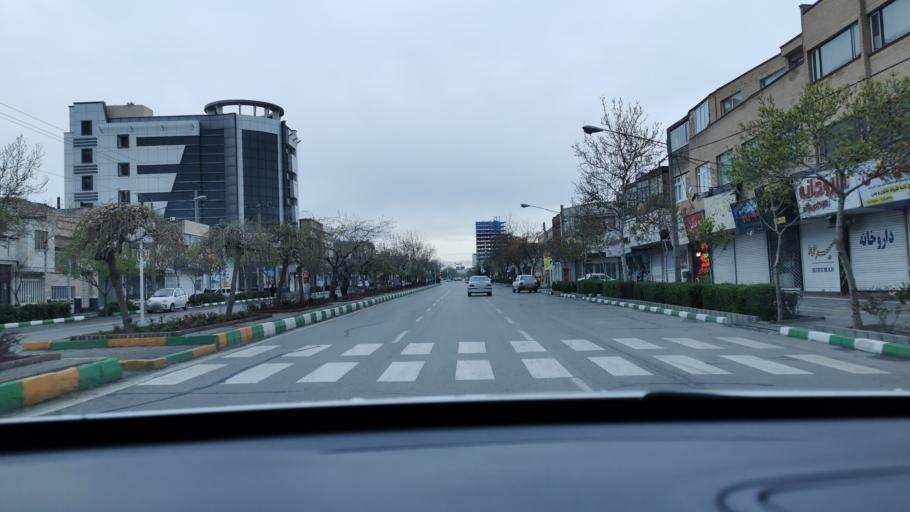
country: IR
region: Razavi Khorasan
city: Mashhad
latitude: 36.3302
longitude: 59.5227
